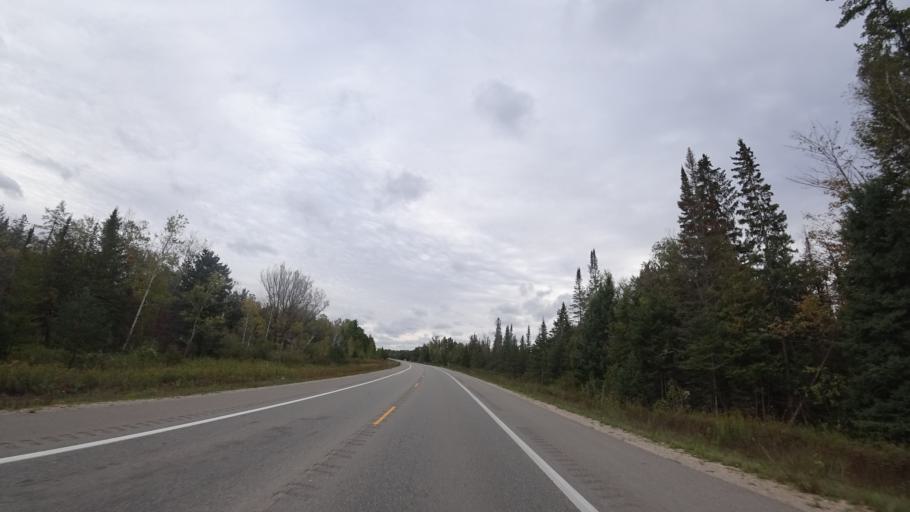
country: US
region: Michigan
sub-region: Charlevoix County
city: Boyne City
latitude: 45.1560
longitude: -84.9197
